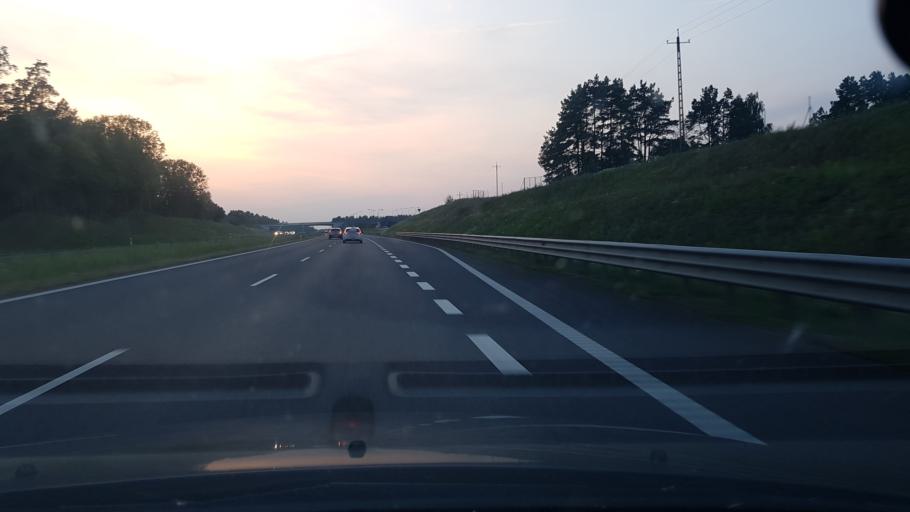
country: PL
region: Warmian-Masurian Voivodeship
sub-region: Powiat olsztynski
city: Olsztynek
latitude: 53.5120
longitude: 20.3019
